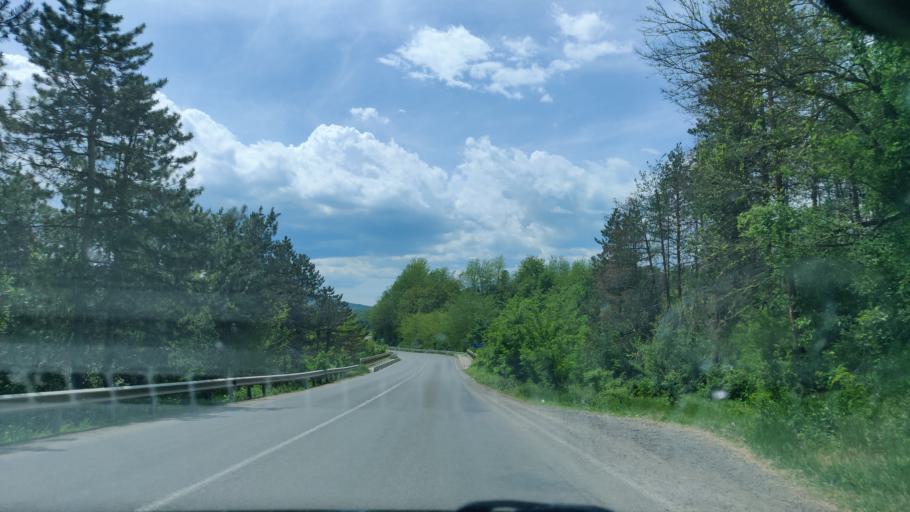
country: RO
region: Vrancea
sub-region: Comuna Vidra
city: Vidra
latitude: 45.8996
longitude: 26.8859
